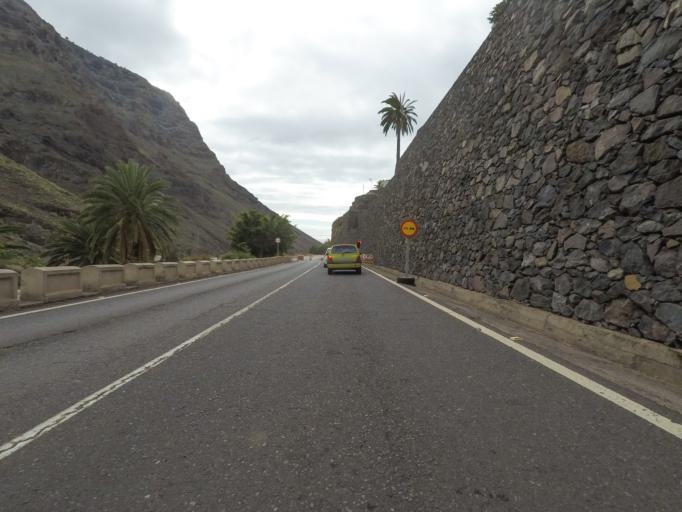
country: ES
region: Canary Islands
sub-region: Provincia de Santa Cruz de Tenerife
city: Alajero
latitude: 28.1039
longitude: -17.3279
